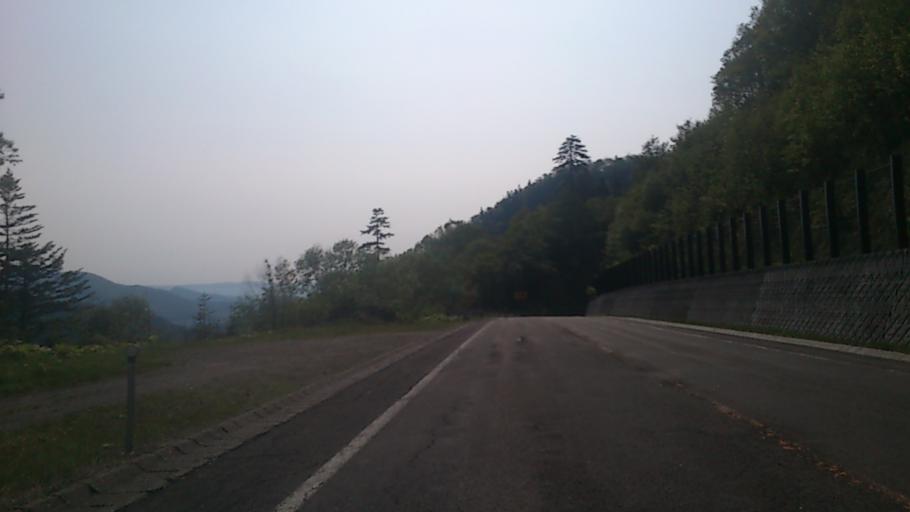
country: JP
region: Hokkaido
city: Bihoro
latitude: 43.4608
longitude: 144.2437
